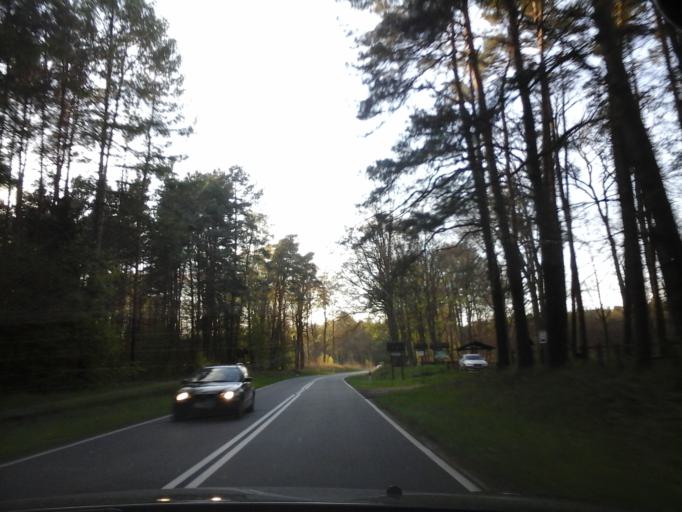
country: PL
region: West Pomeranian Voivodeship
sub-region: Powiat choszczenski
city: Bierzwnik
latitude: 53.0704
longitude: 15.6531
